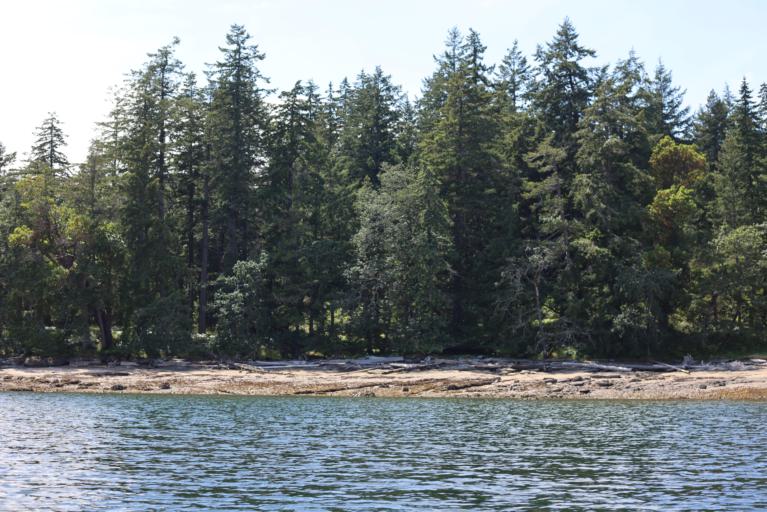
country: CA
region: British Columbia
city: Nanaimo
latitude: 49.1815
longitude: -123.9332
